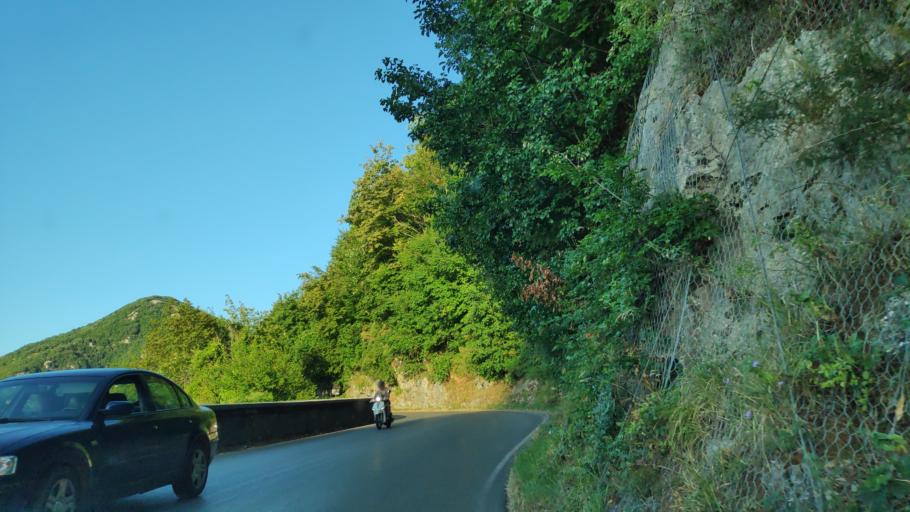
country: IT
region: Campania
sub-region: Provincia di Salerno
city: Corbara
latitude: 40.7189
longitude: 14.6081
